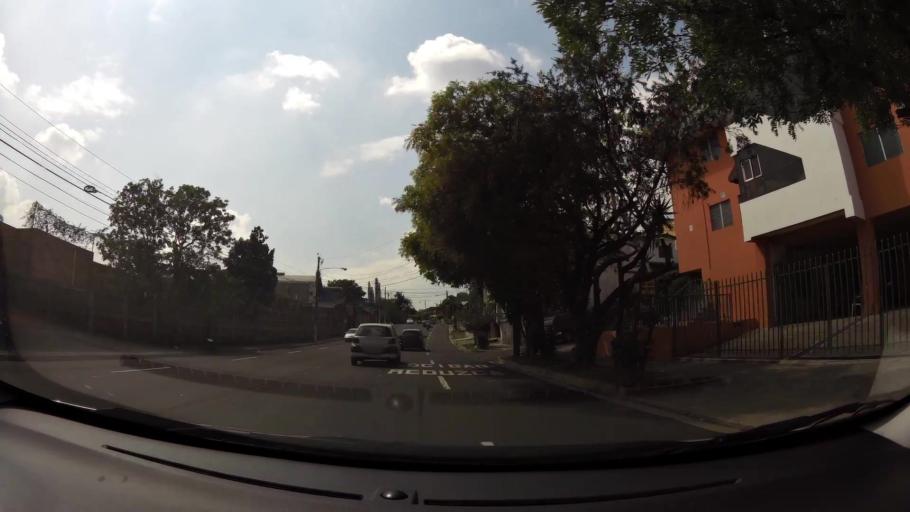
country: SV
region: San Salvador
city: Mejicanos
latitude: 13.7094
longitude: -89.2202
